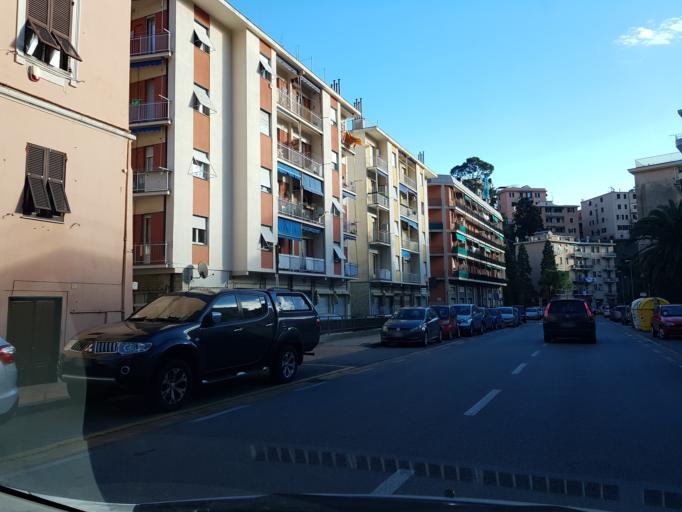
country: IT
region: Liguria
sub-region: Provincia di Genova
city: Bogliasco
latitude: 44.3878
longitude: 9.0338
